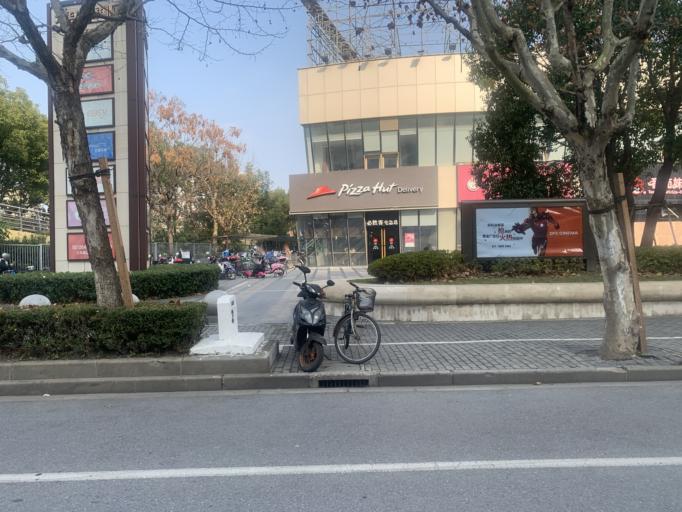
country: CN
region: Shanghai Shi
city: Huamu
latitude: 31.1818
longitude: 121.5170
